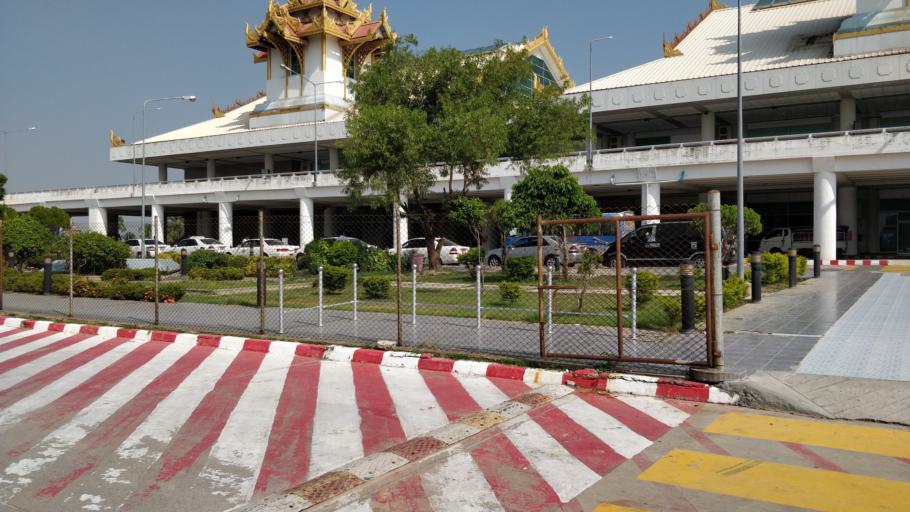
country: MM
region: Sagain
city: Sagaing
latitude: 21.7051
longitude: 95.9691
